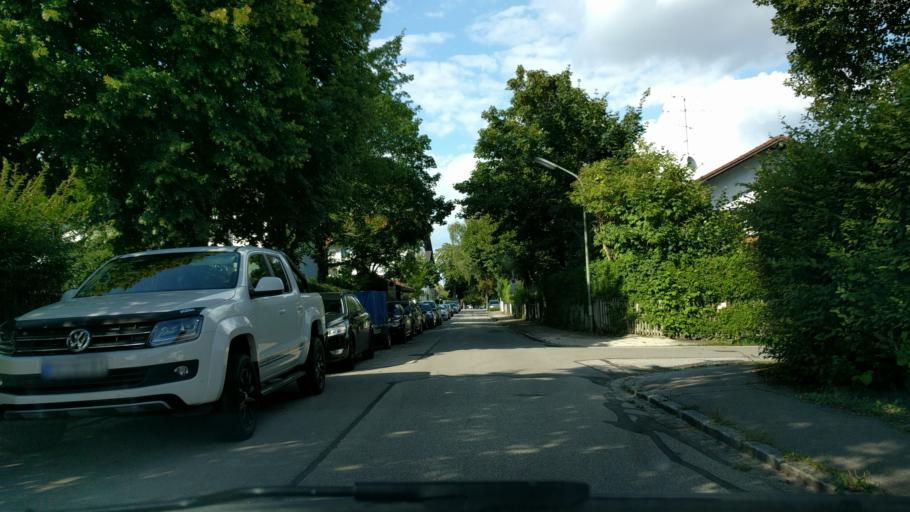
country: DE
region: Bavaria
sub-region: Upper Bavaria
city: Oberhaching
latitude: 48.0181
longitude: 11.5864
